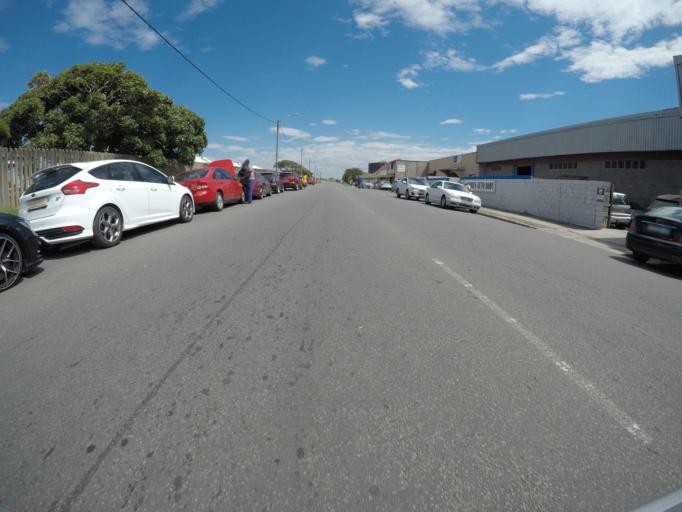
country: ZA
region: Eastern Cape
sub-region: Buffalo City Metropolitan Municipality
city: East London
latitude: -33.0305
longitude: 27.9082
